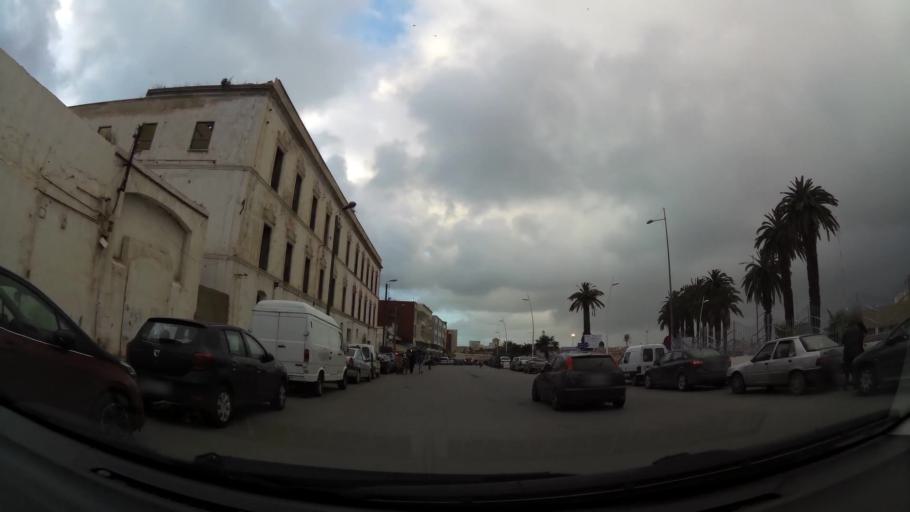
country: MA
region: Doukkala-Abda
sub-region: El-Jadida
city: El Jadida
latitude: 33.2528
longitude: -8.5021
